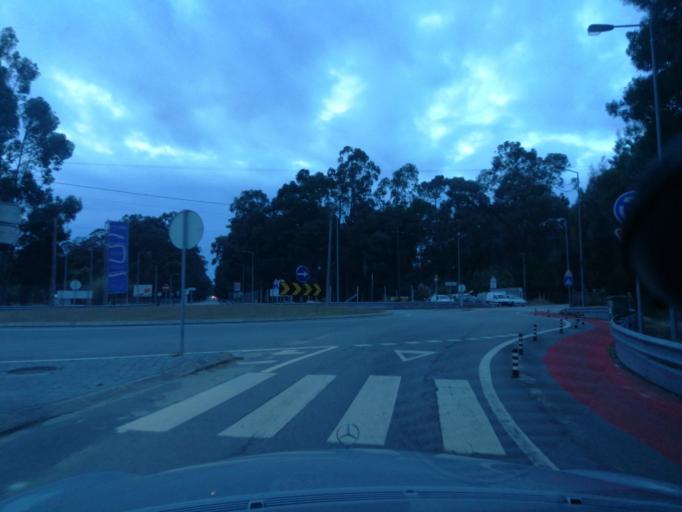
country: PT
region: Aveiro
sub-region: Murtosa
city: Murtosa
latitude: 40.7619
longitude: -8.6234
